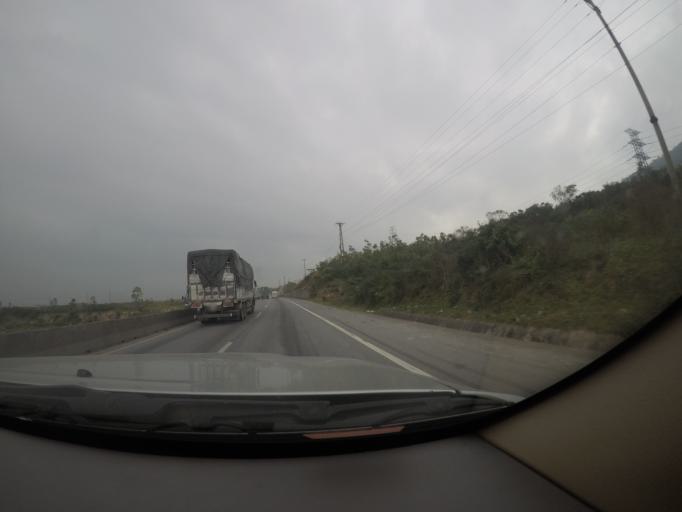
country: VN
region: Ha Tinh
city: Ky Anh
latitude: 17.9957
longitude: 106.4609
